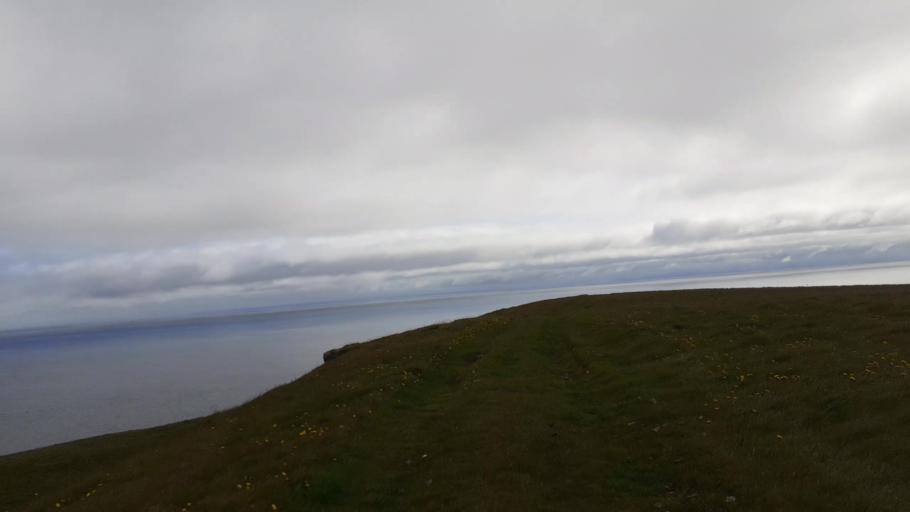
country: IS
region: Northeast
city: Dalvik
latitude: 66.5380
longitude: -17.9821
